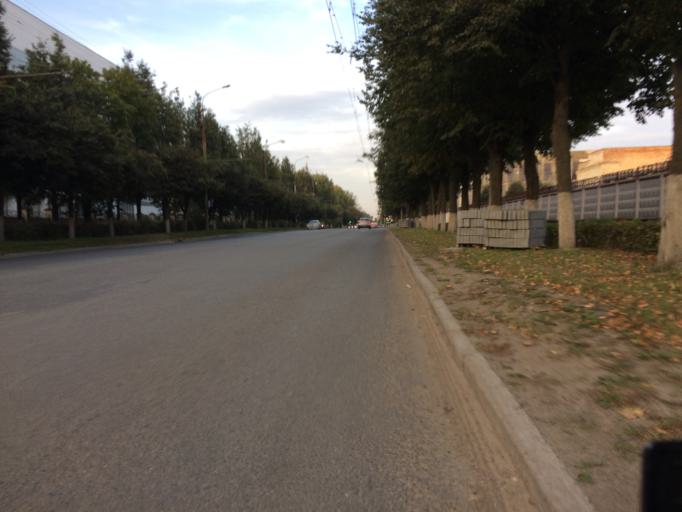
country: RU
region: Mariy-El
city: Yoshkar-Ola
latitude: 56.6351
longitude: 47.8608
